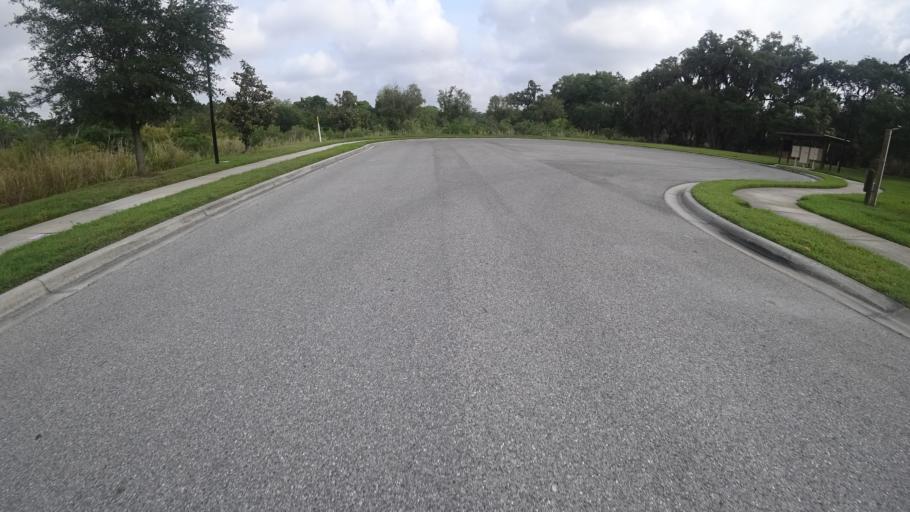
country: US
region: Florida
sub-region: Manatee County
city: Samoset
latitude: 27.4323
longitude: -82.5181
